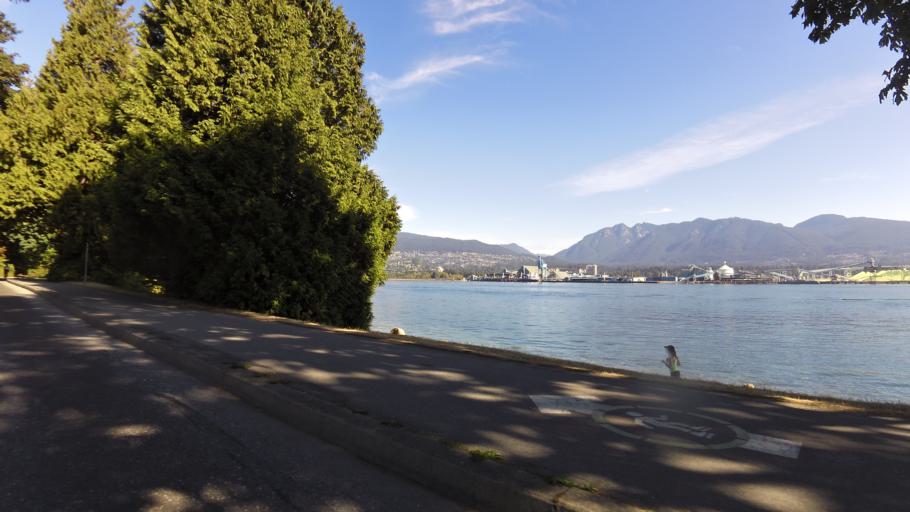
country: CA
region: British Columbia
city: West End
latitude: 49.3006
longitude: -123.1237
